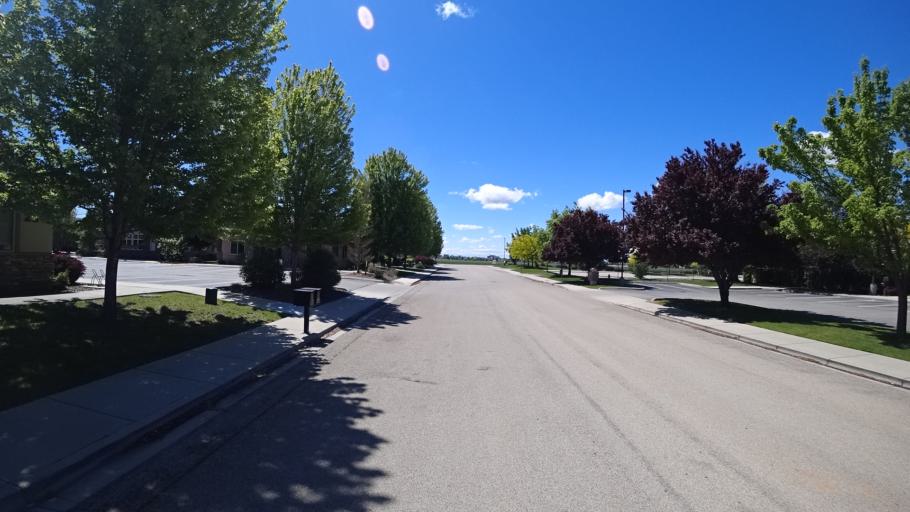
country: US
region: Idaho
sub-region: Ada County
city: Meridian
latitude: 43.6277
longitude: -116.3560
